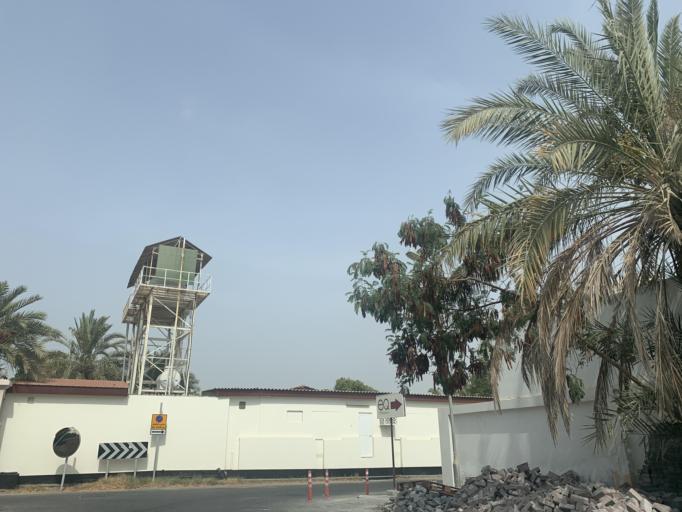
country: BH
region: Manama
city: Jidd Hafs
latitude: 26.1990
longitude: 50.4771
